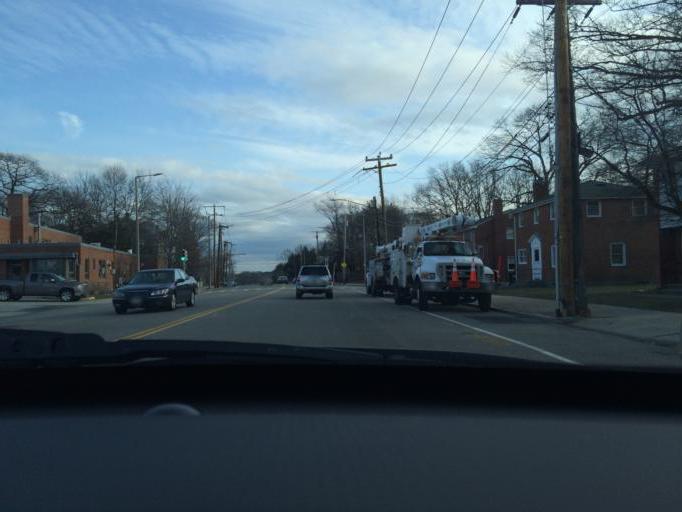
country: US
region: Massachusetts
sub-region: Norfolk County
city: Milton
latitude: 42.2785
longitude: -71.0797
